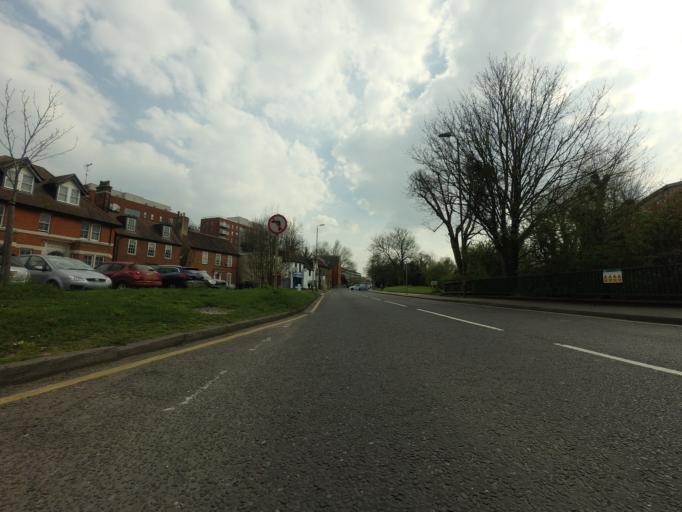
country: GB
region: England
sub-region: Greater London
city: Orpington
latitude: 51.3934
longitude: 0.1144
